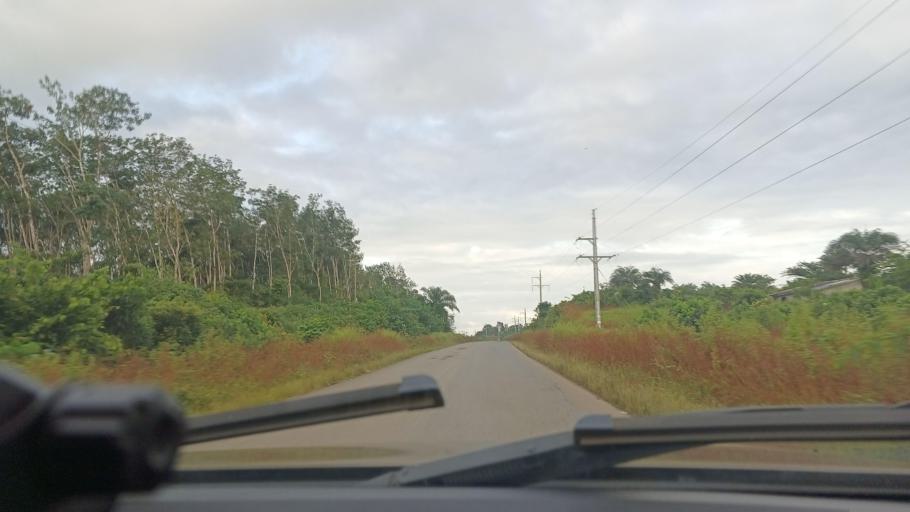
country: LR
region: Montserrado
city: Monrovia
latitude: 6.5552
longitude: -10.8666
